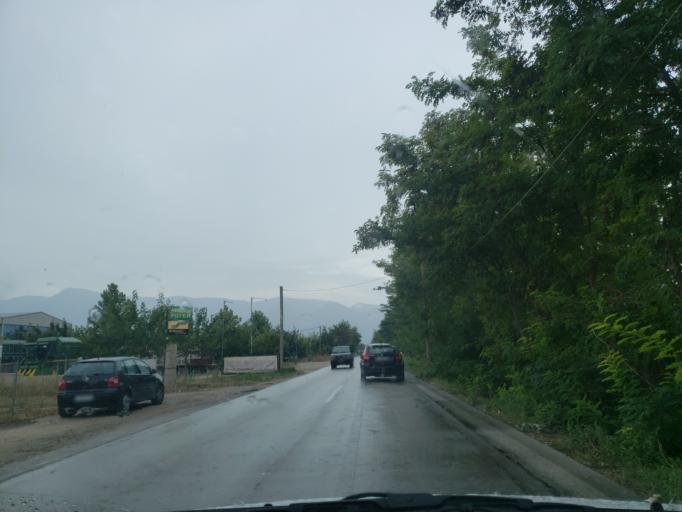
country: GR
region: Central Greece
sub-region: Nomos Fthiotidos
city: Anthili
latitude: 38.8410
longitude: 22.4410
